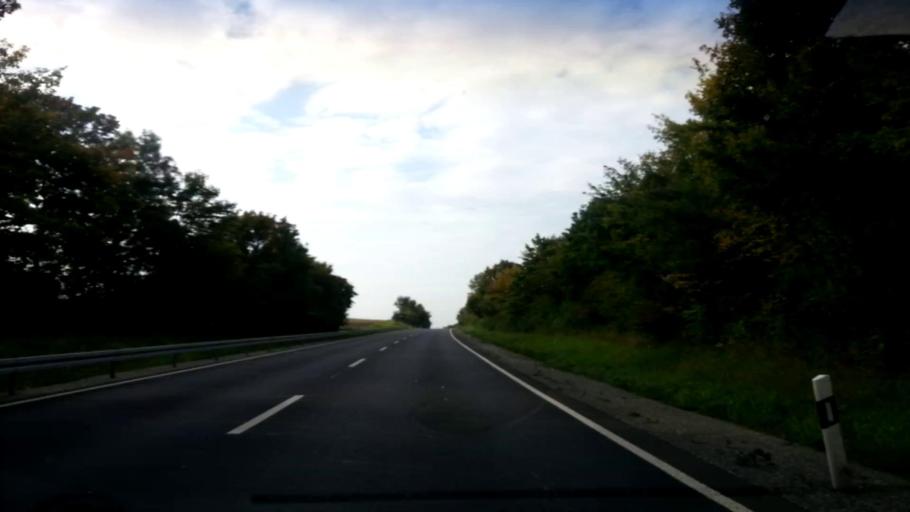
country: DE
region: Bavaria
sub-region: Regierungsbezirk Unterfranken
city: Gerolzhofen
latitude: 49.8969
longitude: 10.3606
